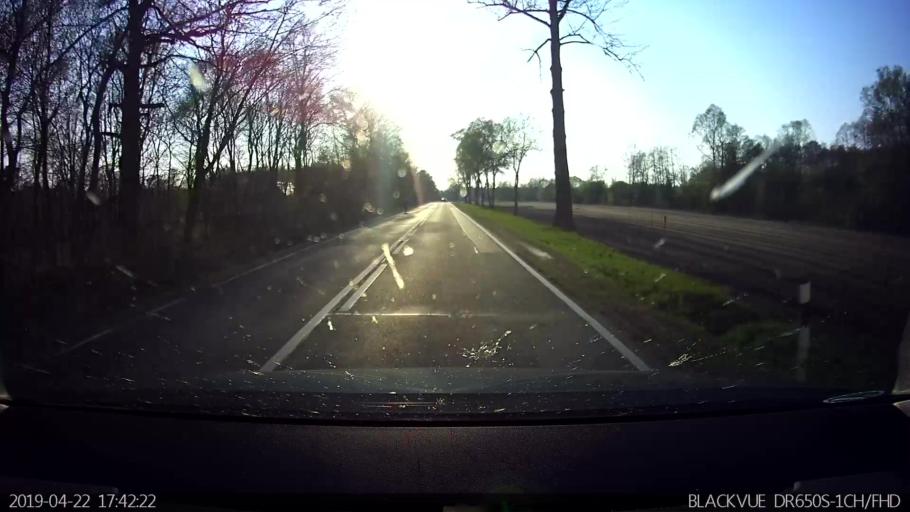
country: PL
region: Masovian Voivodeship
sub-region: Powiat wegrowski
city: Miedzna
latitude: 52.4040
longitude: 22.0808
